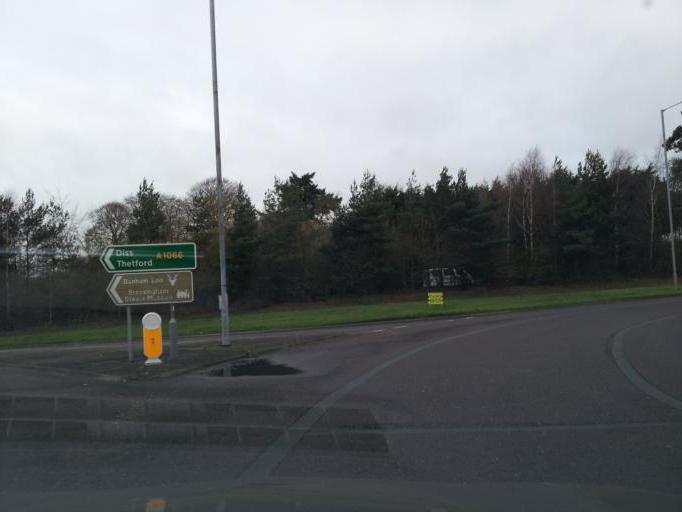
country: GB
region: England
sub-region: Norfolk
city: Diss
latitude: 52.3661
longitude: 1.1512
